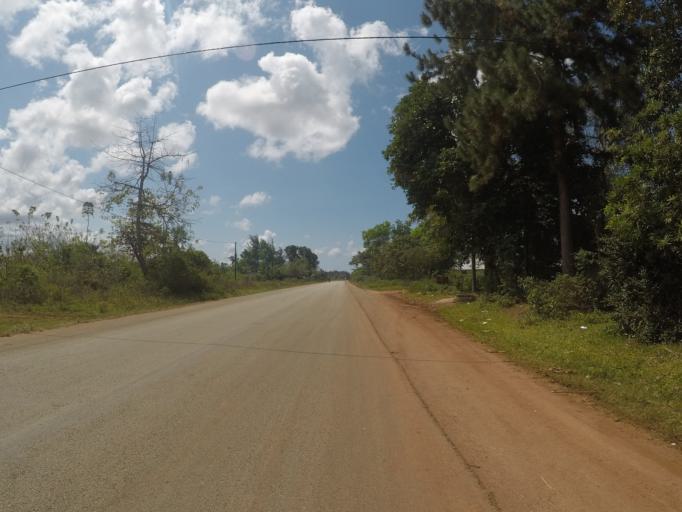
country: TZ
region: Zanzibar Central/South
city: Koani
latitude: -6.1653
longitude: 39.3302
